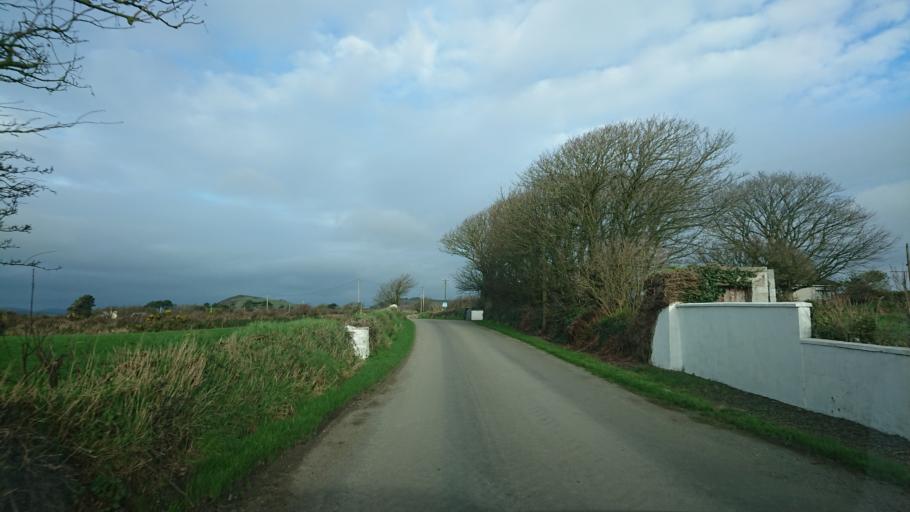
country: IE
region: Munster
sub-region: Waterford
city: Tra Mhor
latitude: 52.1502
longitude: -7.2123
